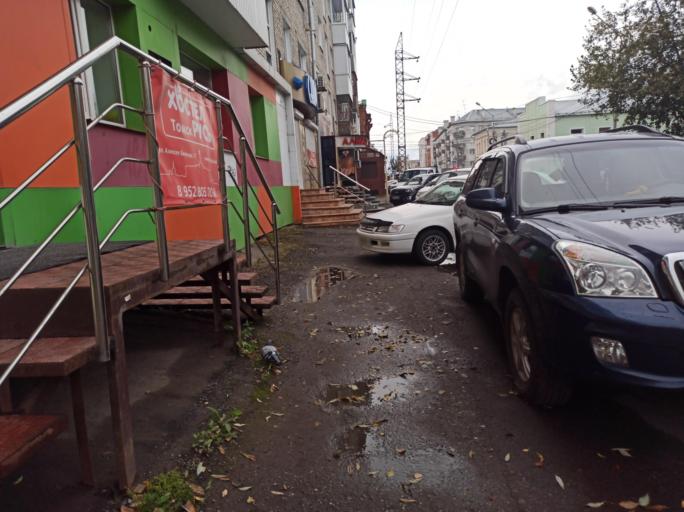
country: RU
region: Tomsk
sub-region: Tomskiy Rayon
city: Tomsk
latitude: 56.4815
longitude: 84.9513
